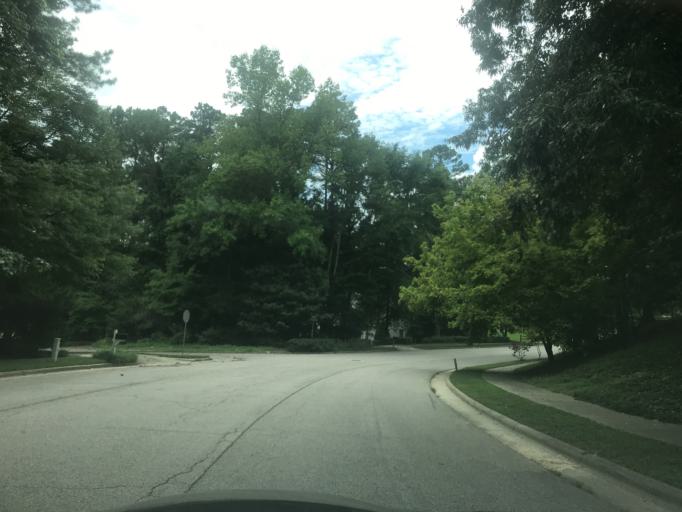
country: US
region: North Carolina
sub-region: Wake County
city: West Raleigh
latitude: 35.8849
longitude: -78.6102
